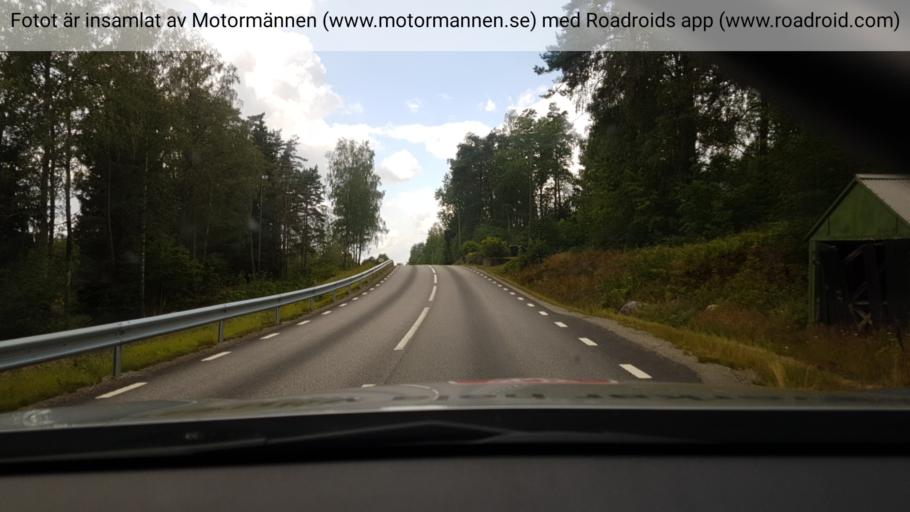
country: SE
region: Vaestra Goetaland
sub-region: Svenljunga Kommun
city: Svenljunga
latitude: 57.4651
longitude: 13.1961
